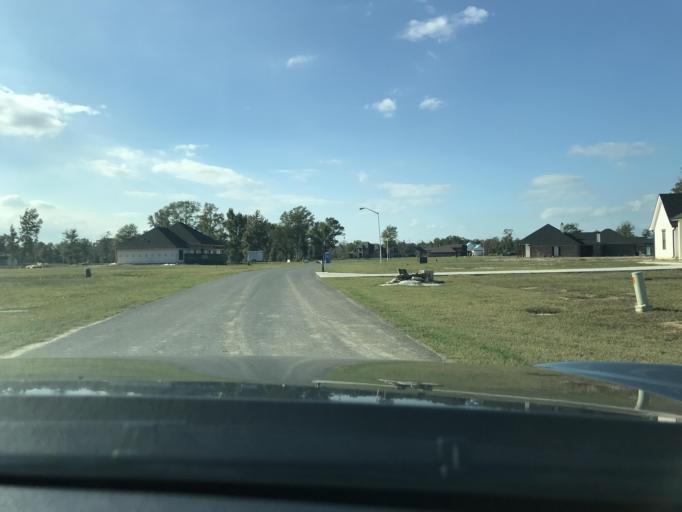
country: US
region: Louisiana
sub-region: Calcasieu Parish
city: Moss Bluff
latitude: 30.3336
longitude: -93.2480
